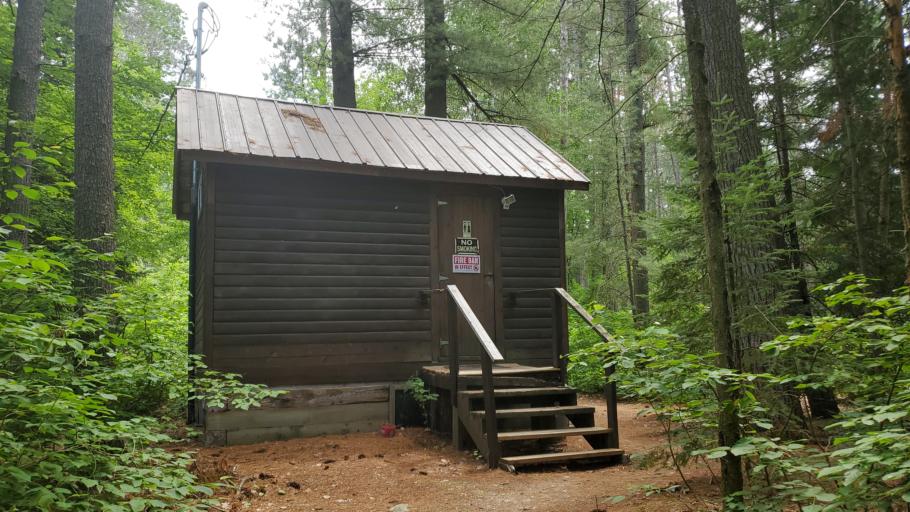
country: CA
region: Ontario
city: Mattawa
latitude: 46.2569
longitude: -78.2760
